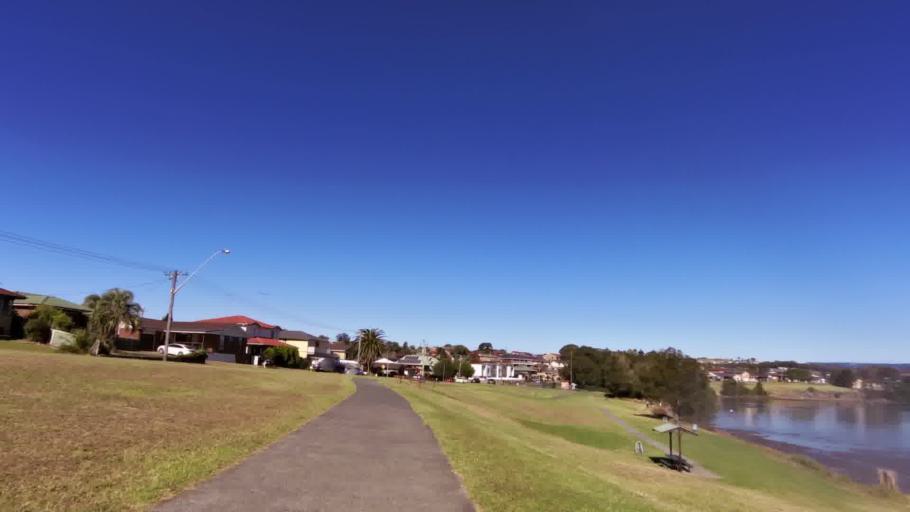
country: AU
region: New South Wales
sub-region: Shellharbour
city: Lake Illawarra
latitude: -34.5495
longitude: 150.8368
